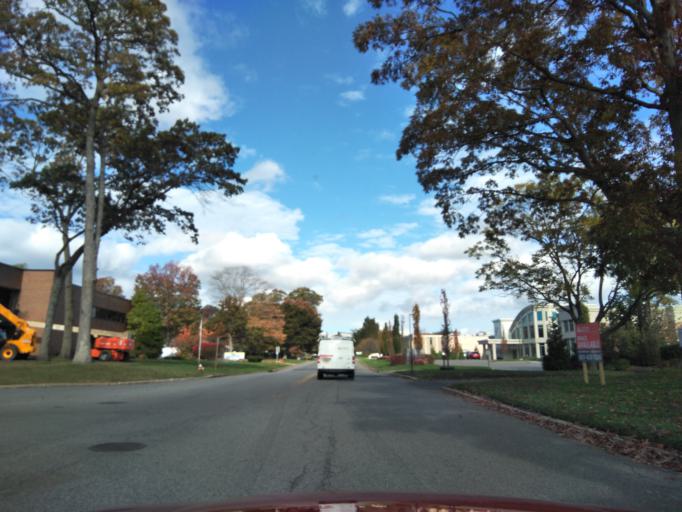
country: US
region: New York
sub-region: Nassau County
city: Syosset
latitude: 40.8064
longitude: -73.4877
